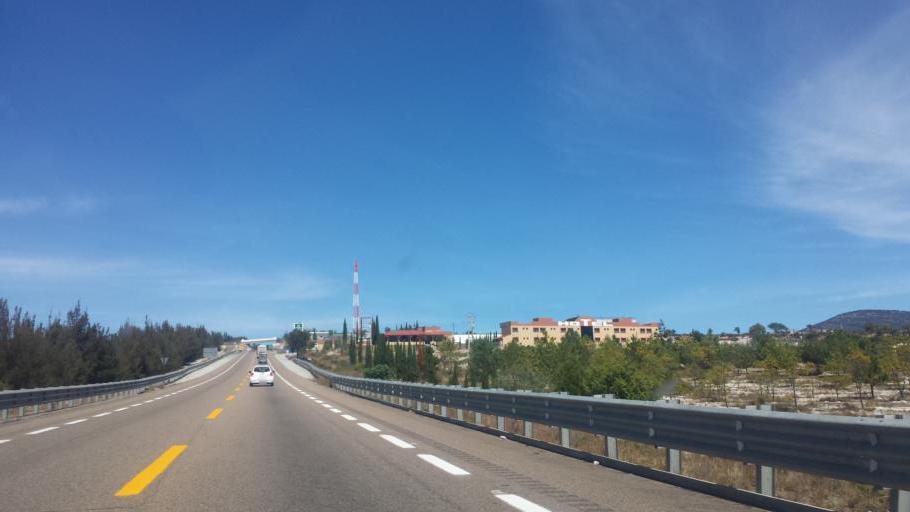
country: MX
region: Oaxaca
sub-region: Villa Tejupam de la Union
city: Villa Tejupam de la Union
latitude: 17.8774
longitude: -97.3747
